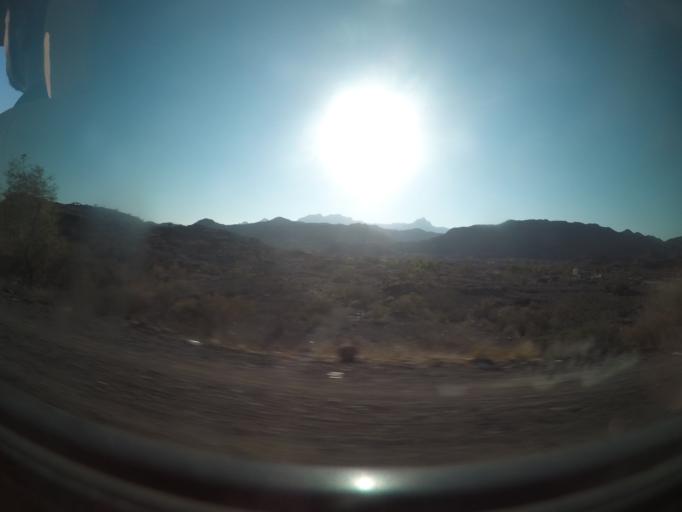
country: YE
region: Lahij
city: Habil ar Raydah
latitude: 13.6558
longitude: 44.8442
